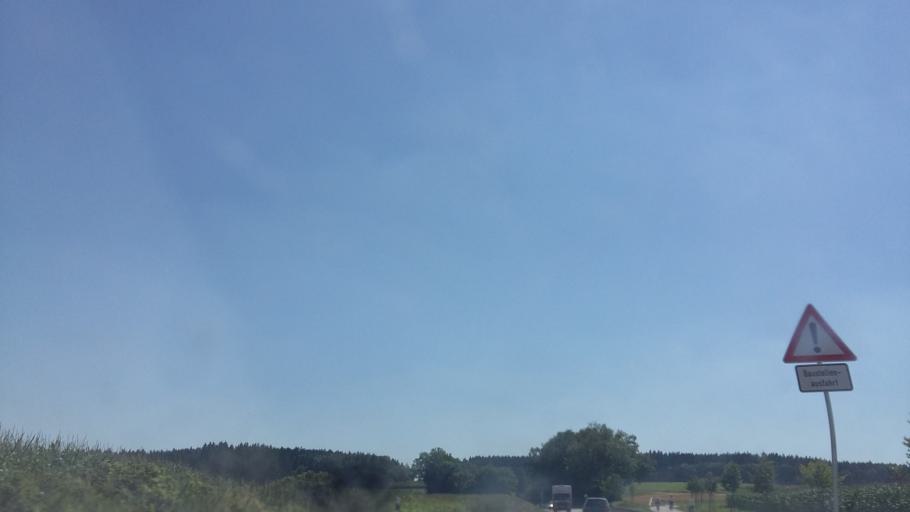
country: DE
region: Bavaria
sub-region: Upper Bavaria
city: Emmering
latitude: 48.1634
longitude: 11.2812
